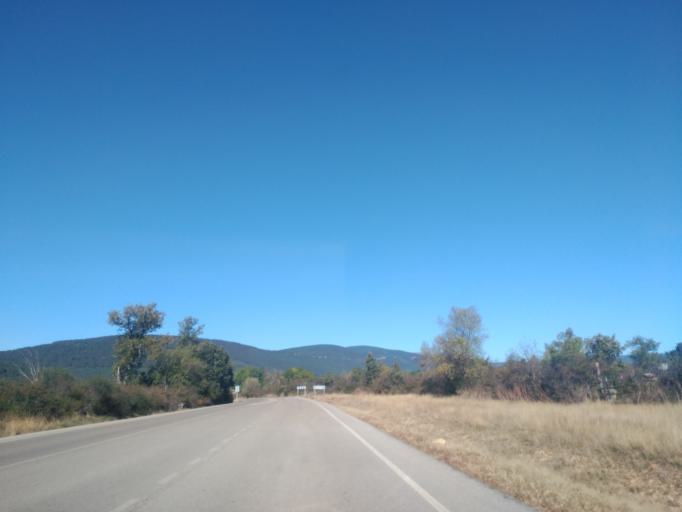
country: ES
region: Castille and Leon
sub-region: Provincia de Soria
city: Vinuesa
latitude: 41.9100
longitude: -2.7511
